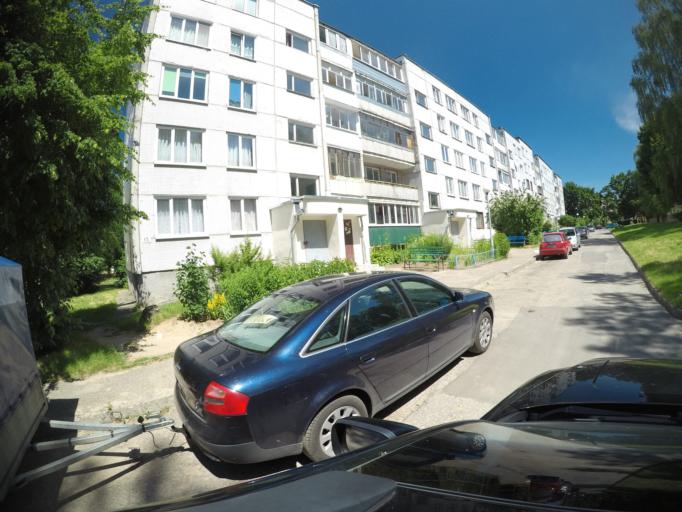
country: BY
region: Grodnenskaya
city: Hrodna
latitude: 53.6956
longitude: 23.8161
